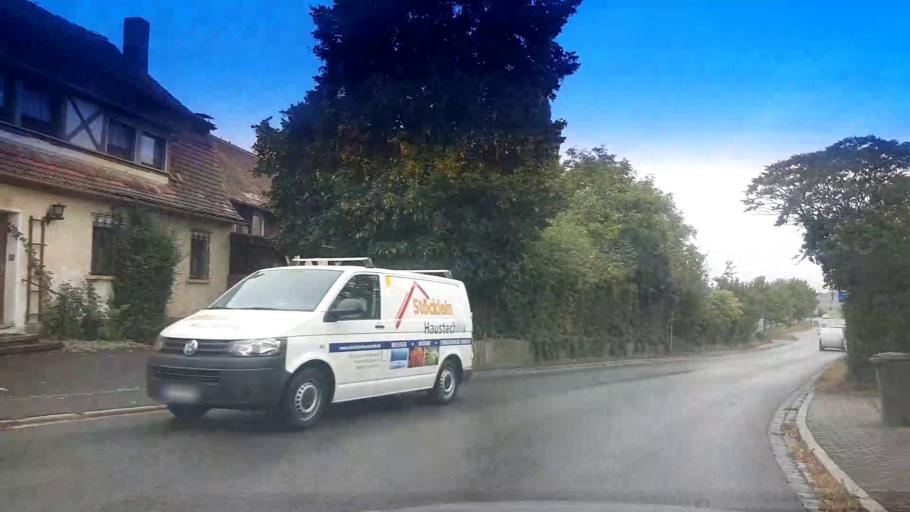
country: DE
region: Bavaria
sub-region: Upper Franconia
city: Eggolsheim
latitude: 49.7868
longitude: 11.0478
